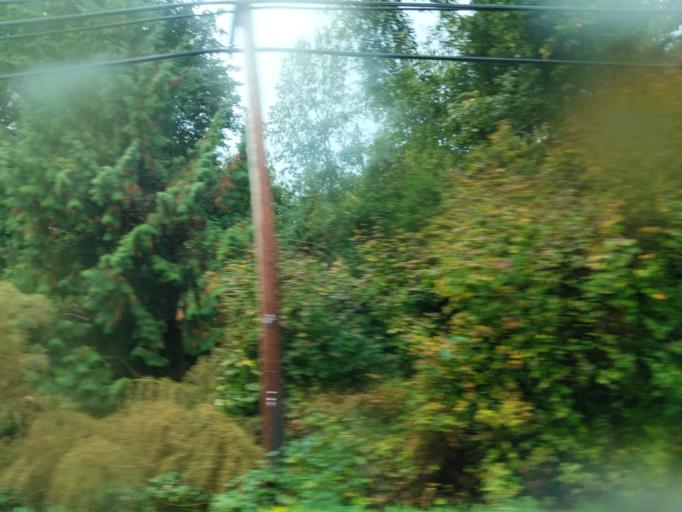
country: US
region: Washington
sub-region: King County
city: Bothell
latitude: 47.7861
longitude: -122.2074
